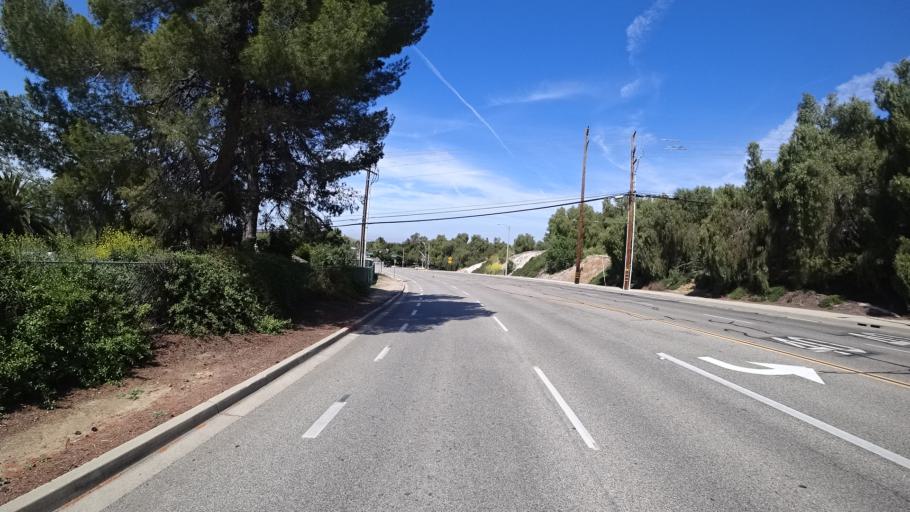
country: US
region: California
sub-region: Ventura County
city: Thousand Oaks
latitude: 34.1992
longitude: -118.8510
